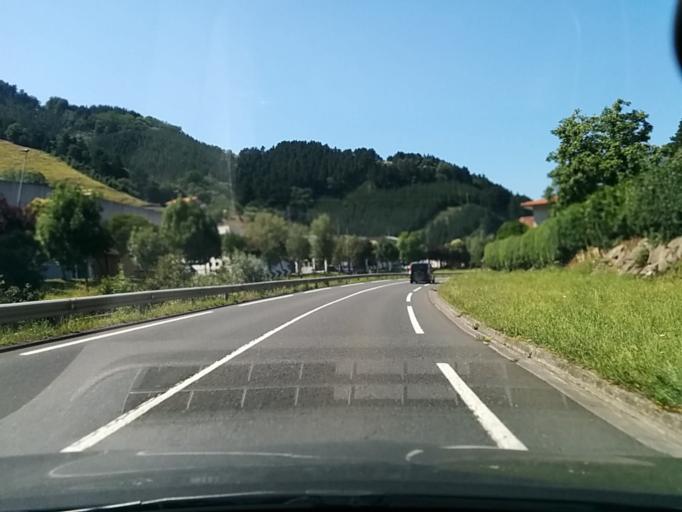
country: ES
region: Basque Country
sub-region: Bizkaia
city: Ondarroa
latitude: 43.3108
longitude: -2.4096
